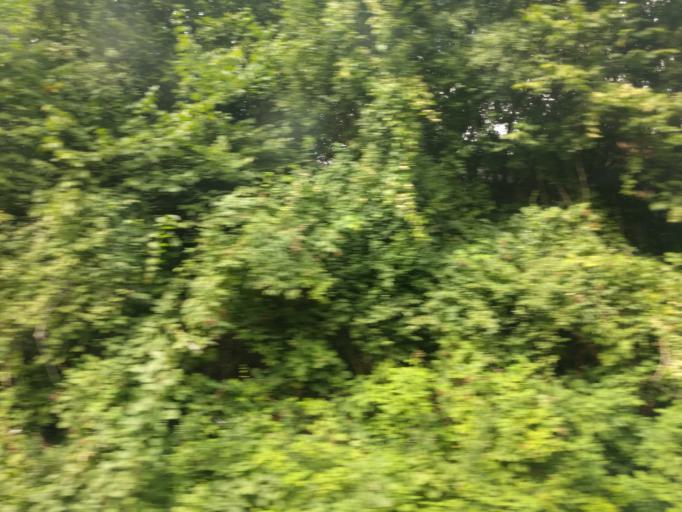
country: DK
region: Zealand
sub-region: Slagelse Kommune
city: Slagelse
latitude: 55.4129
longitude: 11.3648
